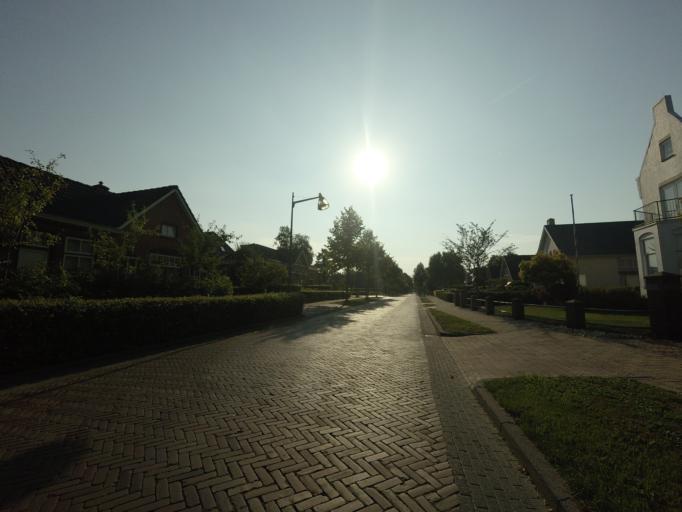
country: NL
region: Groningen
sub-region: Gemeente Groningen
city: Groningen
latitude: 53.1489
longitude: 6.4912
